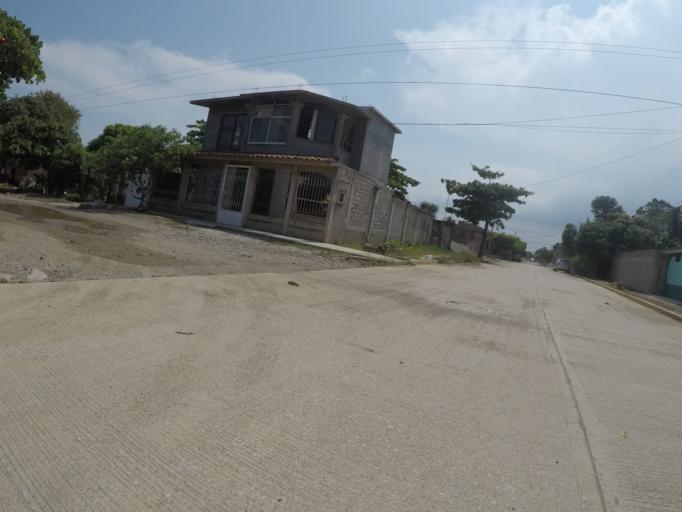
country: MX
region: Oaxaca
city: Union Hidalgo
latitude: 16.4745
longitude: -94.8334
